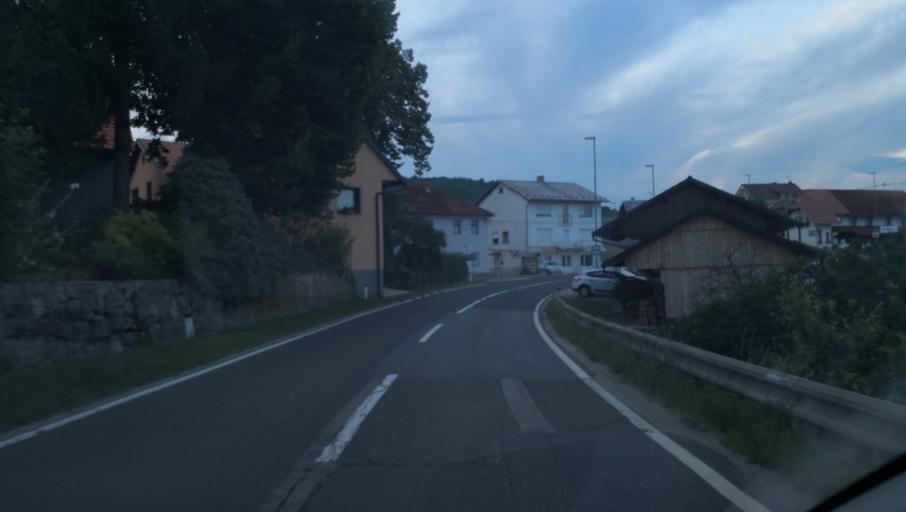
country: SI
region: Metlika
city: Metlika
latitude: 45.6894
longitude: 15.2729
